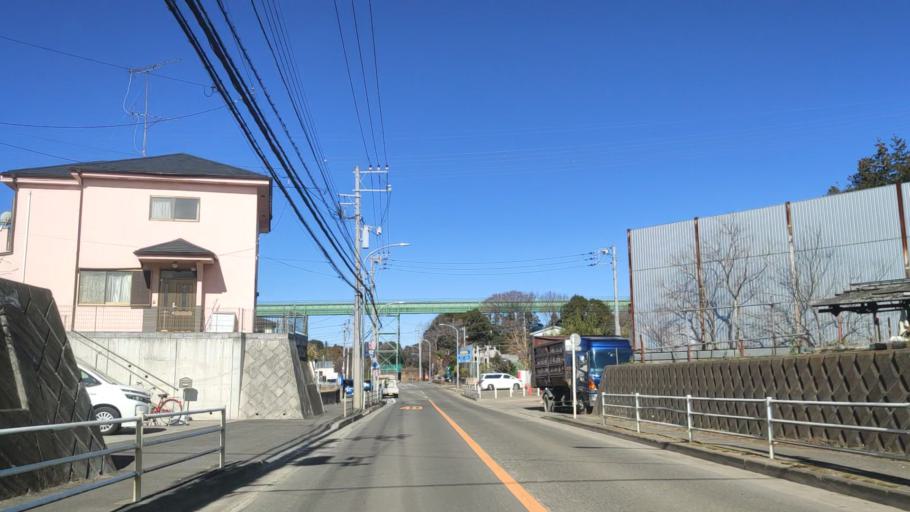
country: JP
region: Kanagawa
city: Minami-rinkan
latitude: 35.4977
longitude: 139.5152
